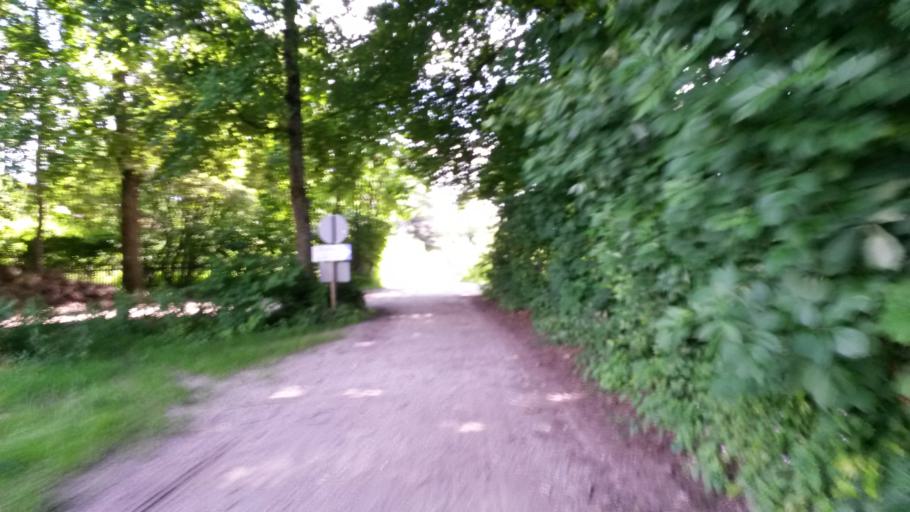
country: DE
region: Bavaria
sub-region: Upper Bavaria
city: Chieming
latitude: 47.9044
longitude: 12.5189
